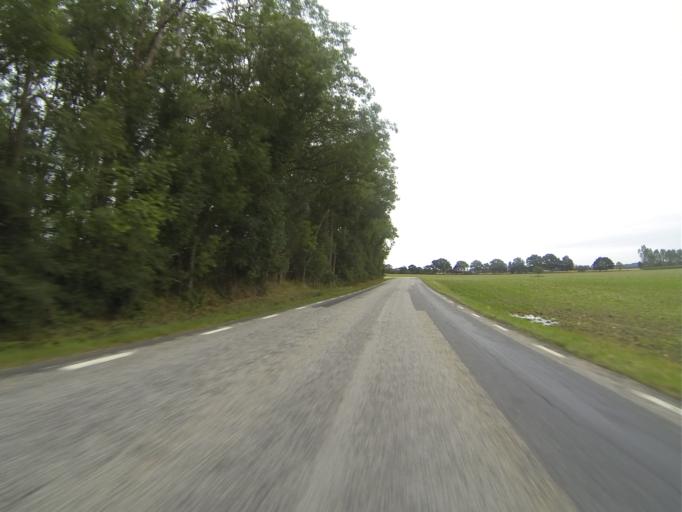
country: SE
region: Skane
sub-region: Lunds Kommun
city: Genarp
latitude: 55.6232
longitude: 13.3977
